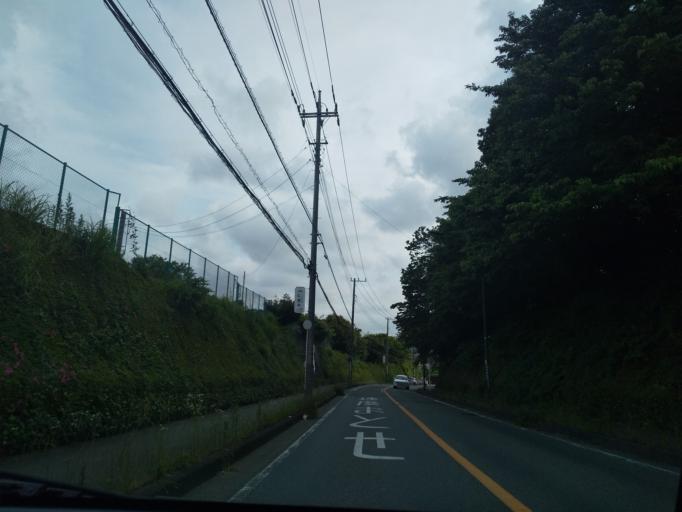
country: JP
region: Kanagawa
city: Zama
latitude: 35.5137
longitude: 139.3891
